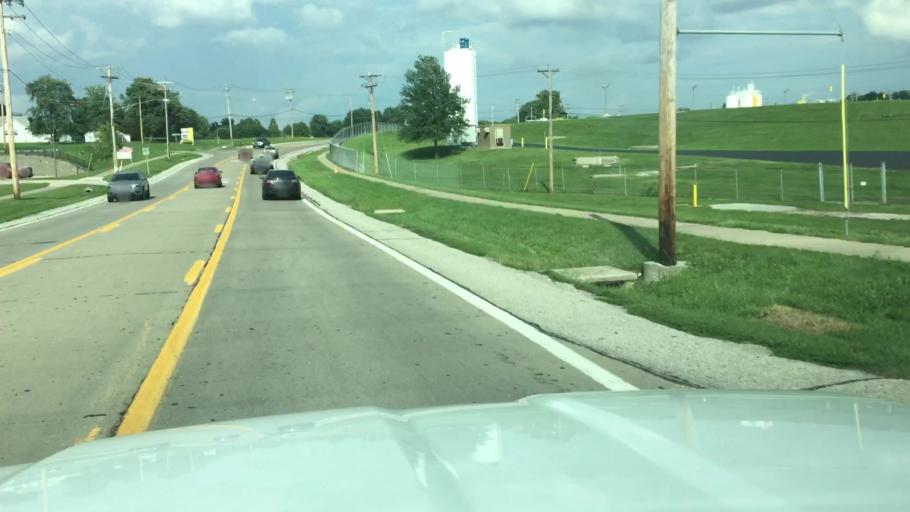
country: US
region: Missouri
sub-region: Jefferson County
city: Arnold
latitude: 38.4620
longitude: -90.3693
